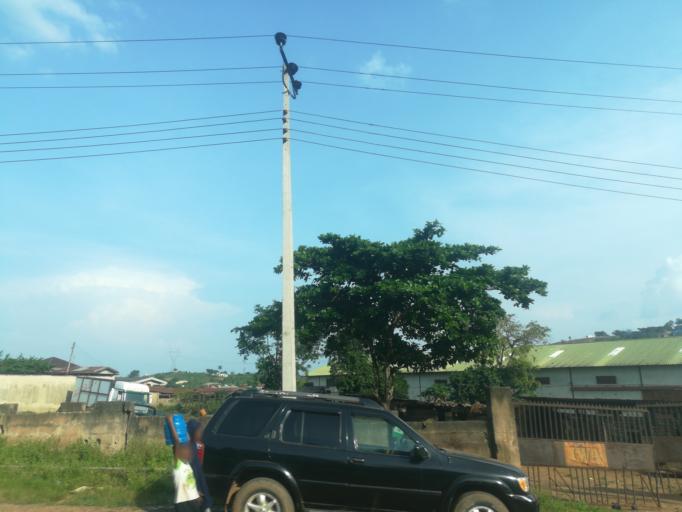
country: NG
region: Oyo
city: Moniya
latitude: 7.4920
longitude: 3.9141
